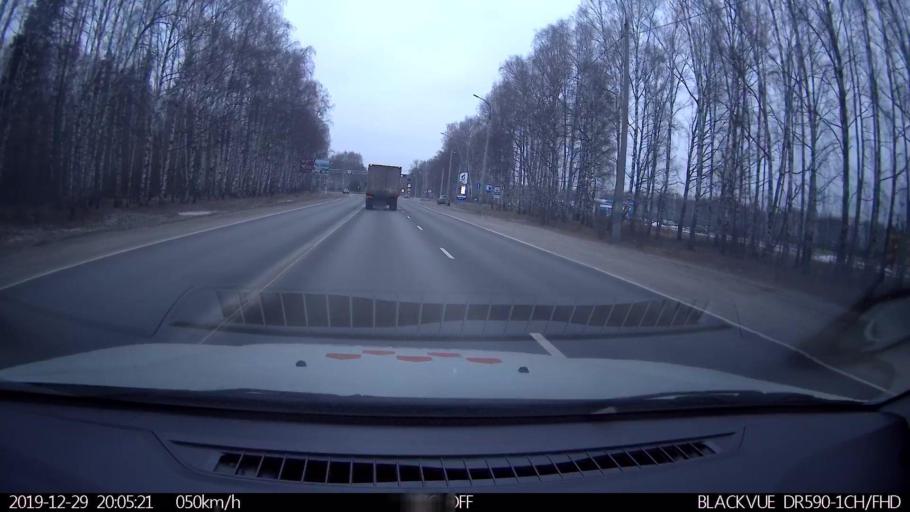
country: RU
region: Nizjnij Novgorod
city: Neklyudovo
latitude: 56.3905
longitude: 44.0108
